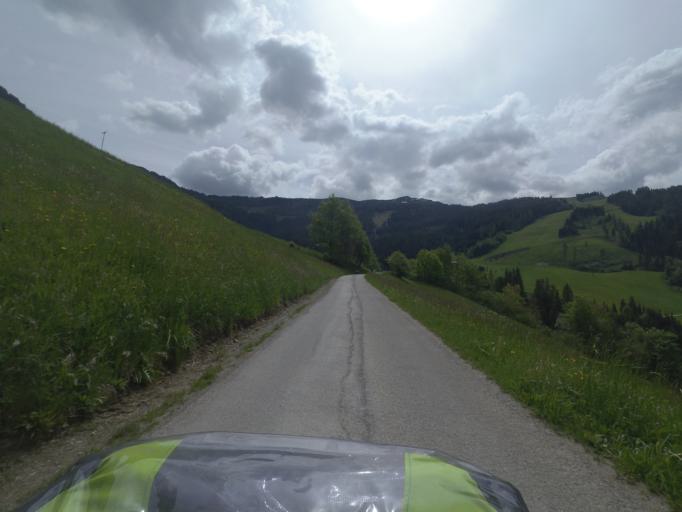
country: AT
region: Salzburg
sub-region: Politischer Bezirk Sankt Johann im Pongau
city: Dorfgastein
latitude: 47.2525
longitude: 13.1230
